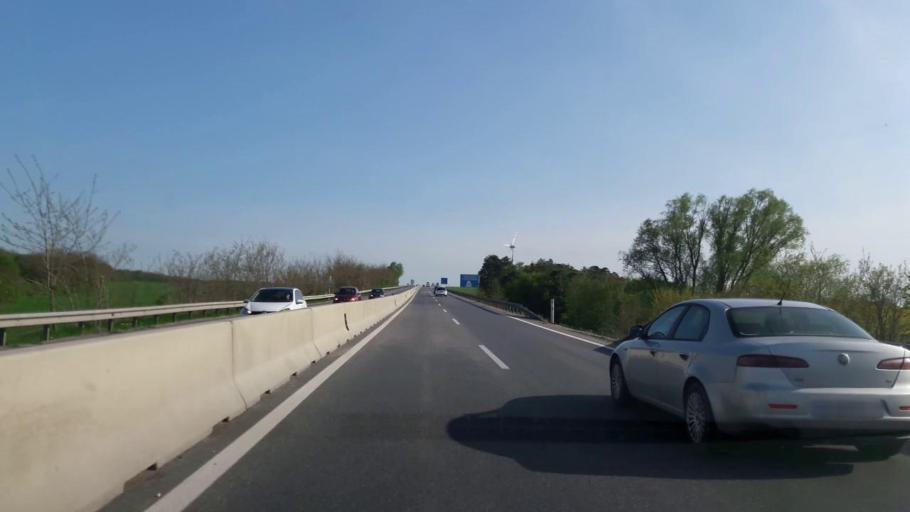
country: AT
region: Lower Austria
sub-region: Politischer Bezirk Hollabrunn
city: Hollabrunn
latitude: 48.5407
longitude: 16.0802
